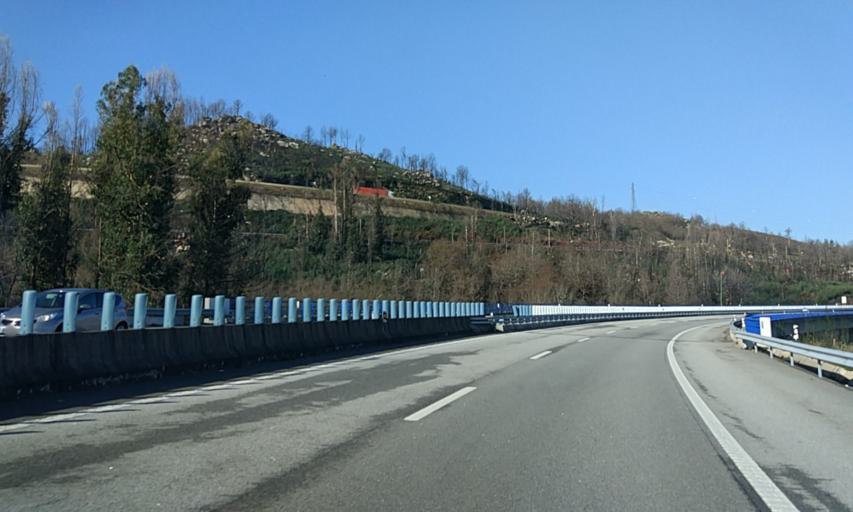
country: PT
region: Viseu
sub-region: Vouzela
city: Vouzela
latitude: 40.7010
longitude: -8.1062
